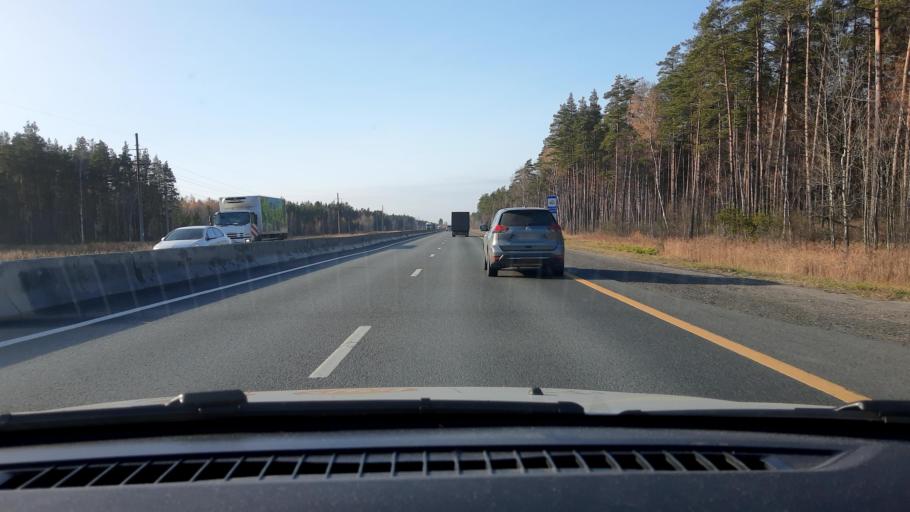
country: RU
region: Nizjnij Novgorod
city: Pyra
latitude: 56.2924
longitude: 43.3295
